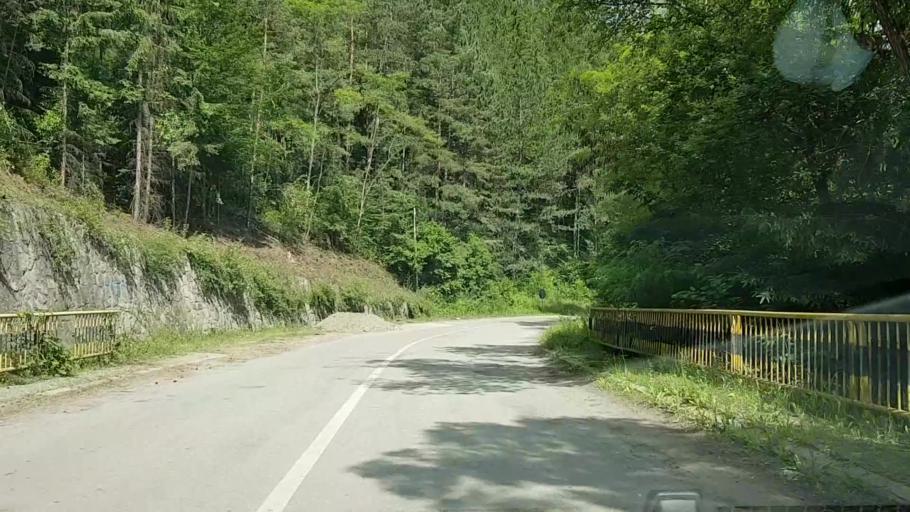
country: RO
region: Neamt
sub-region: Comuna Ceahlau
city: Ceahlau
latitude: 47.0537
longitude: 25.9992
